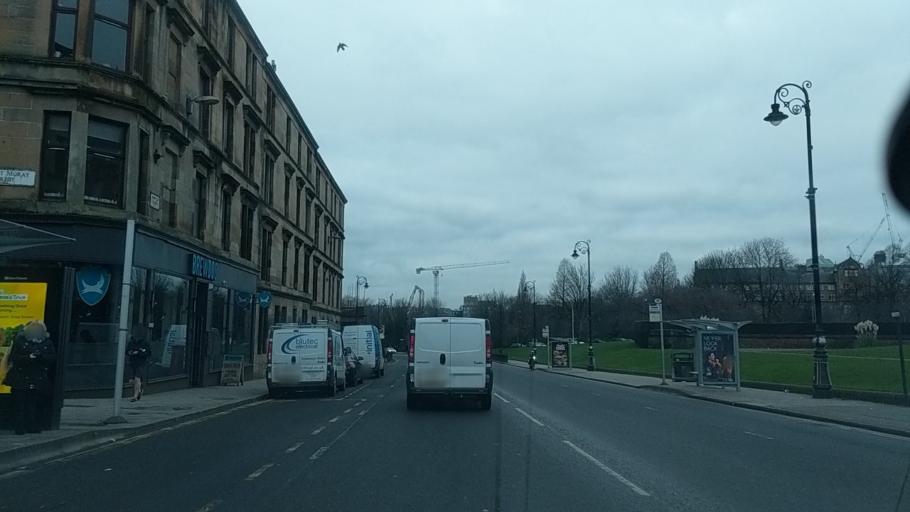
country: GB
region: Scotland
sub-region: Glasgow City
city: Glasgow
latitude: 55.8683
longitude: -4.2920
